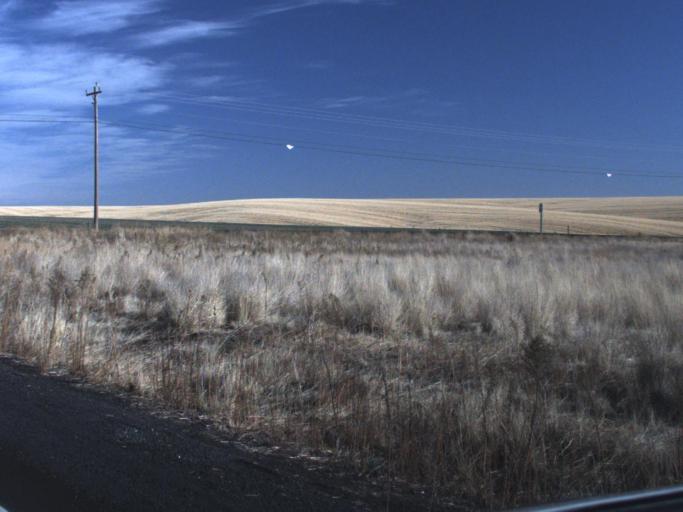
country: US
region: Washington
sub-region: Adams County
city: Ritzville
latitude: 47.1302
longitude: -118.6650
